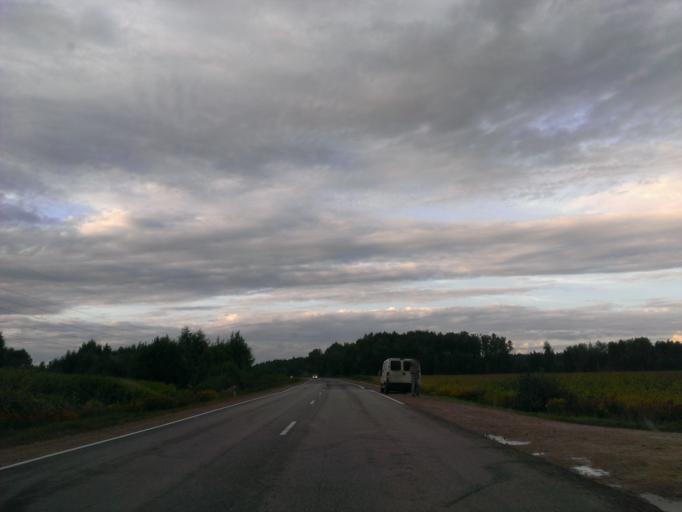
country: LV
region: Salaspils
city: Salaspils
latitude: 56.8618
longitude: 24.4051
